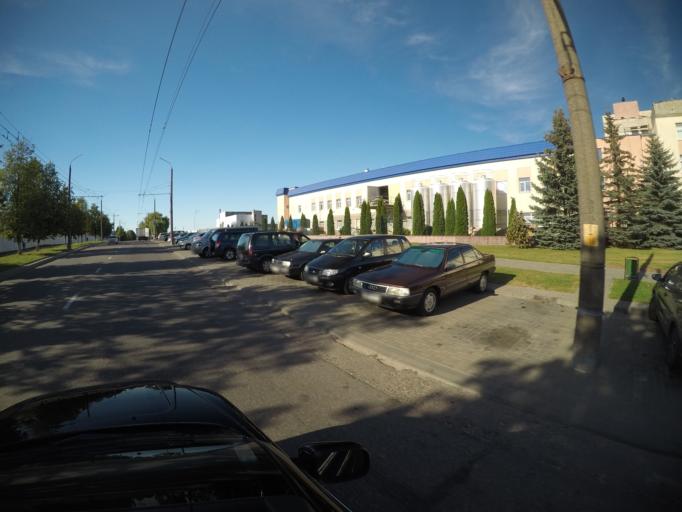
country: BY
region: Grodnenskaya
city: Hrodna
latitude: 53.7091
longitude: 23.8275
